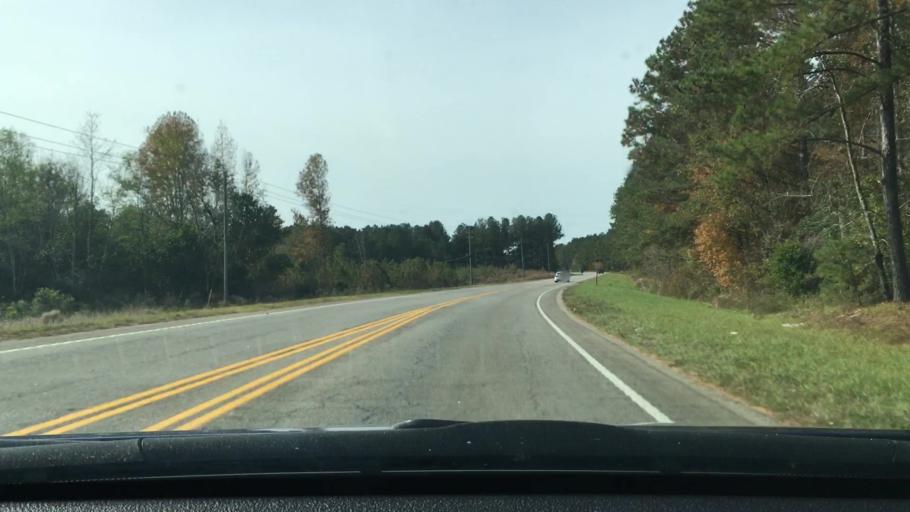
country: US
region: South Carolina
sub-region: Sumter County
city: Cherryvale
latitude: 33.9362
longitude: -80.4435
